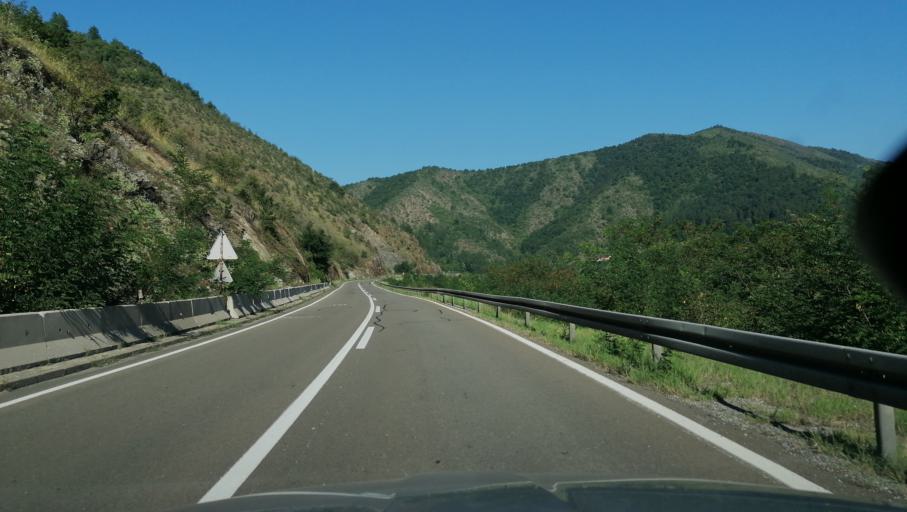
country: RS
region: Central Serbia
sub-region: Raski Okrug
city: Kraljevo
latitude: 43.6599
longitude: 20.5846
